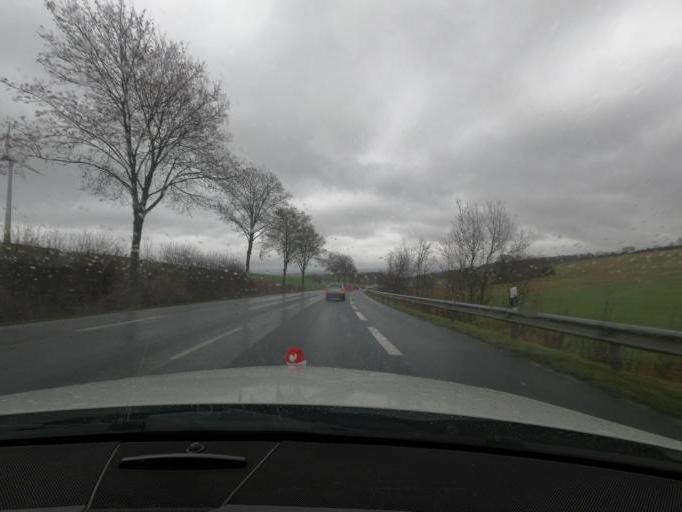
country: DE
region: Lower Saxony
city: Einbeck
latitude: 51.8652
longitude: 9.9050
